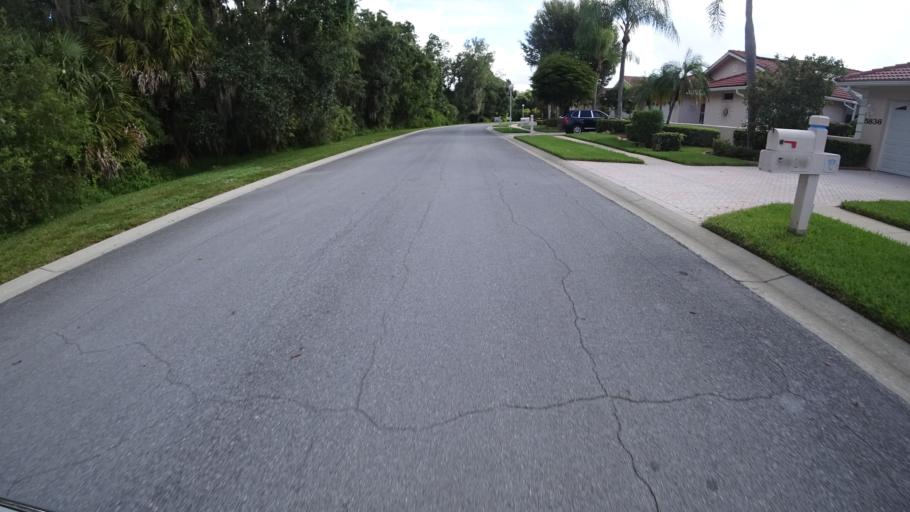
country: US
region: Florida
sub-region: Sarasota County
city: Desoto Lakes
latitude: 27.3961
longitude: -82.4860
